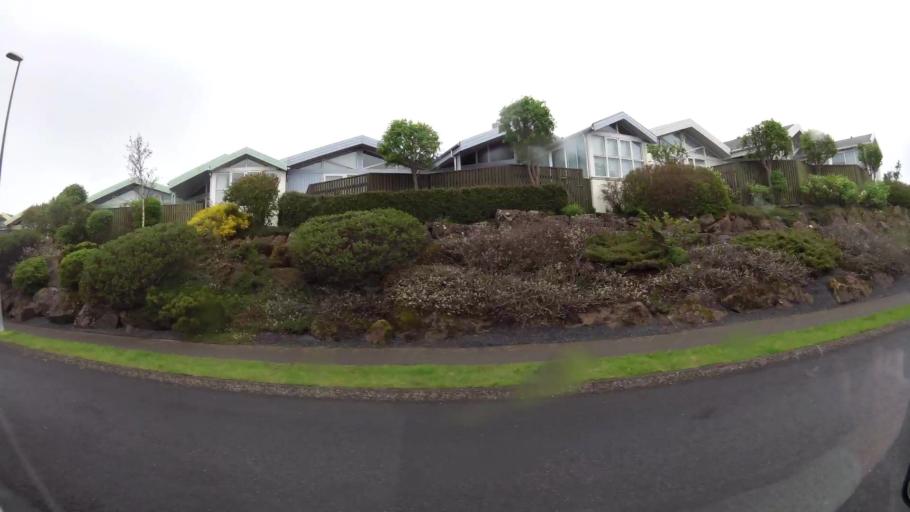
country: IS
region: Capital Region
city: Kopavogur
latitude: 64.0960
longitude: -21.9003
